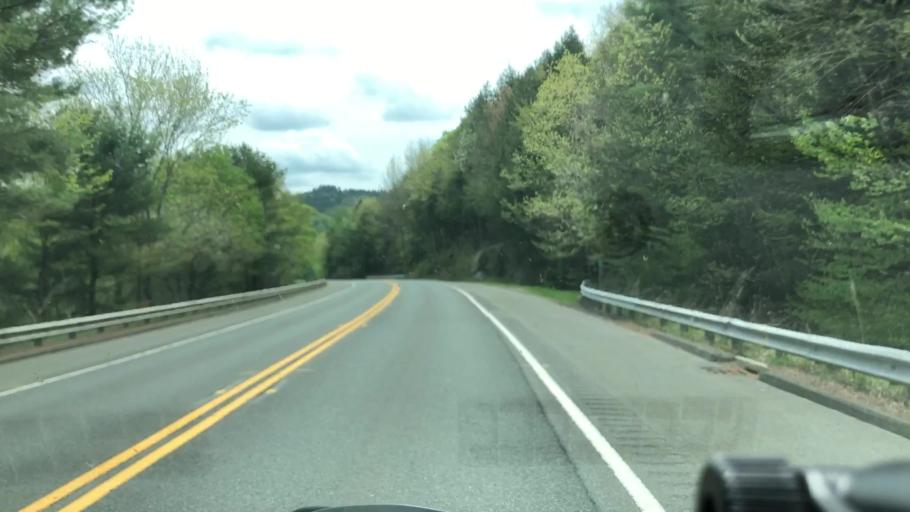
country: US
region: Massachusetts
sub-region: Hampshire County
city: Chesterfield
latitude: 42.4592
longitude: -72.8944
